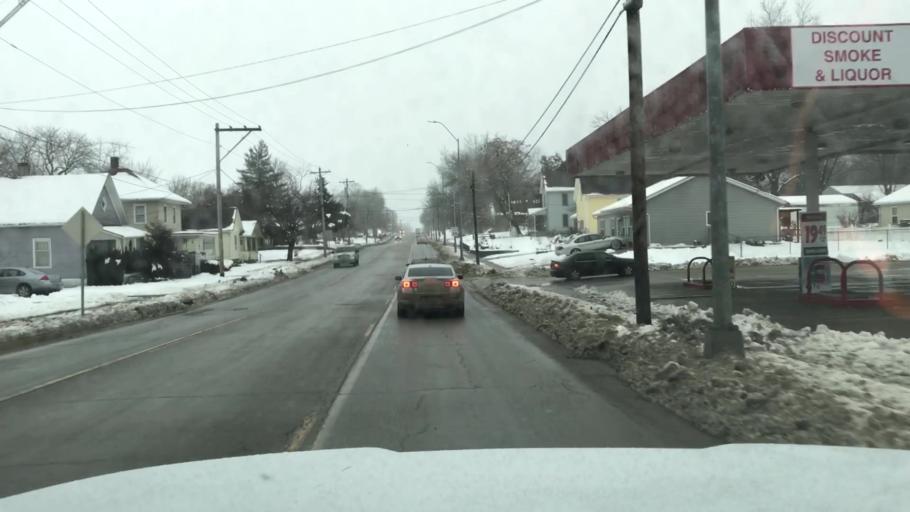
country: US
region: Missouri
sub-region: Clinton County
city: Cameron
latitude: 39.7374
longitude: -94.2360
